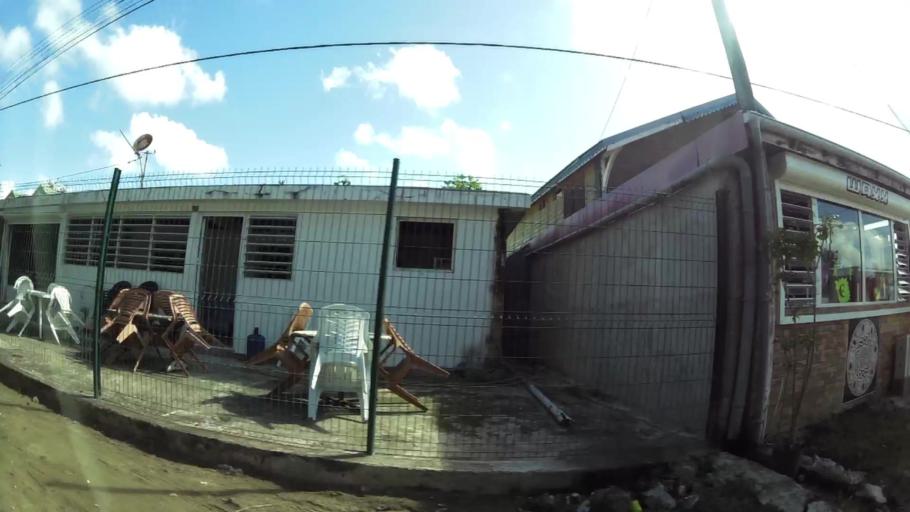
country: GP
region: Guadeloupe
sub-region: Guadeloupe
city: Port-Louis
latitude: 16.4213
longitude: -61.5337
